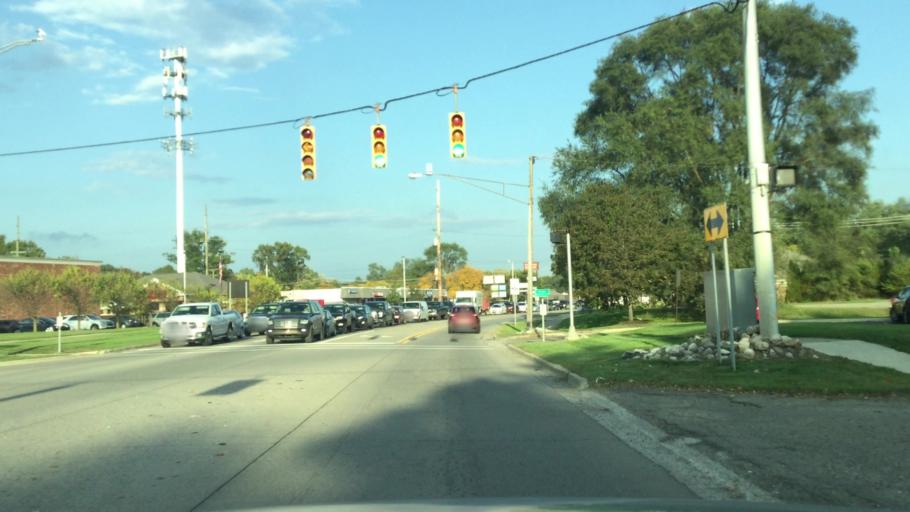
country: US
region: Michigan
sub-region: Oakland County
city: Wolverine Lake
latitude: 42.6146
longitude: -83.4419
